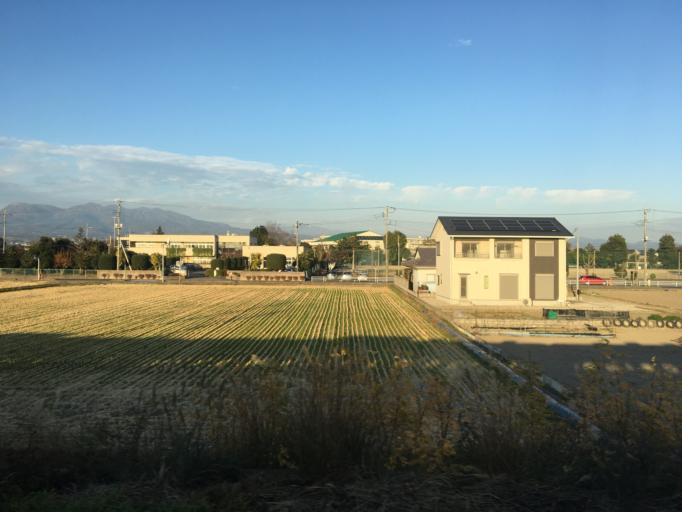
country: JP
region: Gunma
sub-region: Sawa-gun
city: Tamamura
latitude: 36.3610
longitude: 139.1269
